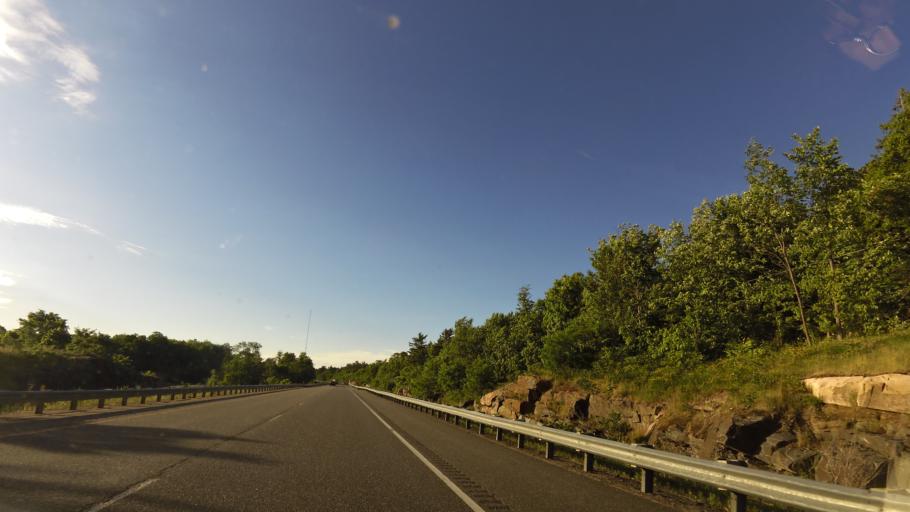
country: CA
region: Ontario
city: Midland
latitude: 44.9474
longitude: -79.7761
